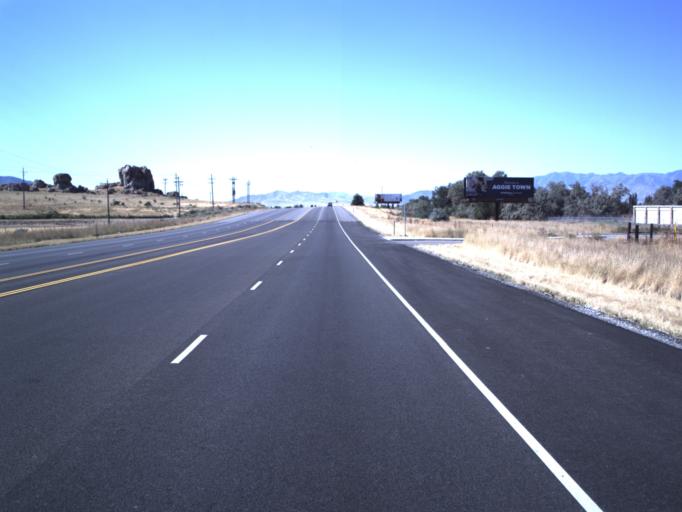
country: US
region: Utah
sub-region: Tooele County
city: Stansbury park
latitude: 40.6648
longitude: -112.2867
